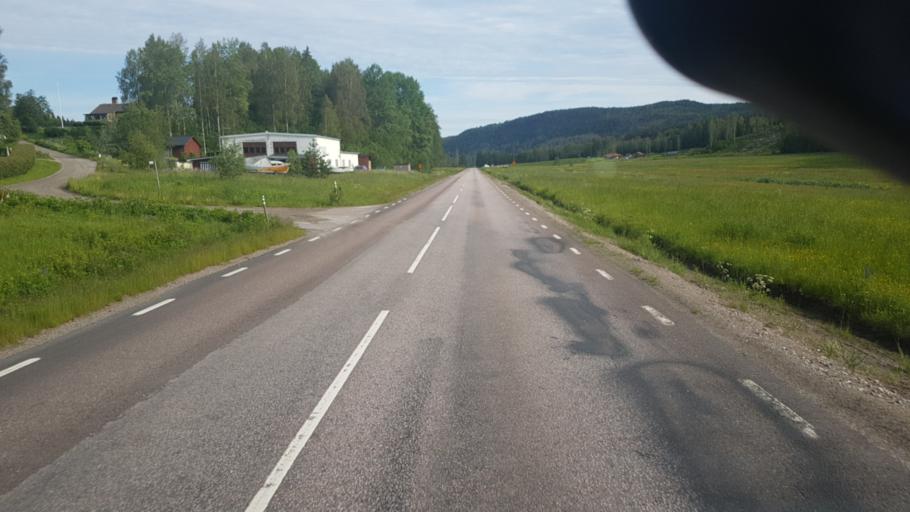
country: SE
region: Vaermland
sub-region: Arvika Kommun
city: Arvika
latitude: 59.7327
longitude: 12.6427
